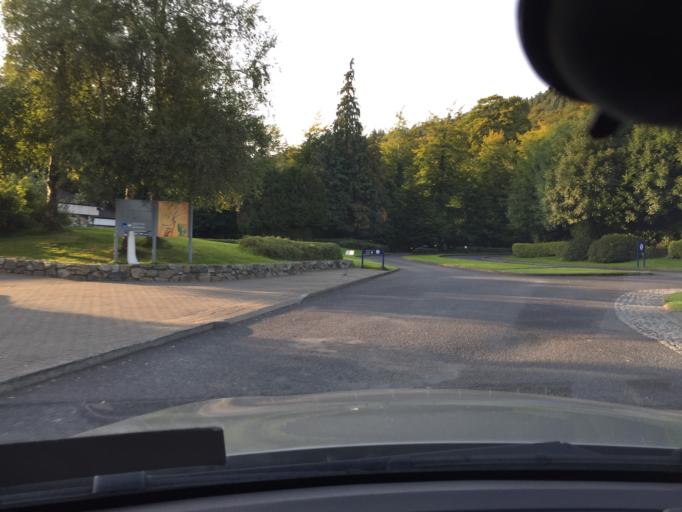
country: IE
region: Leinster
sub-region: Wicklow
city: Rathdrum
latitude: 53.0104
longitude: -6.3237
